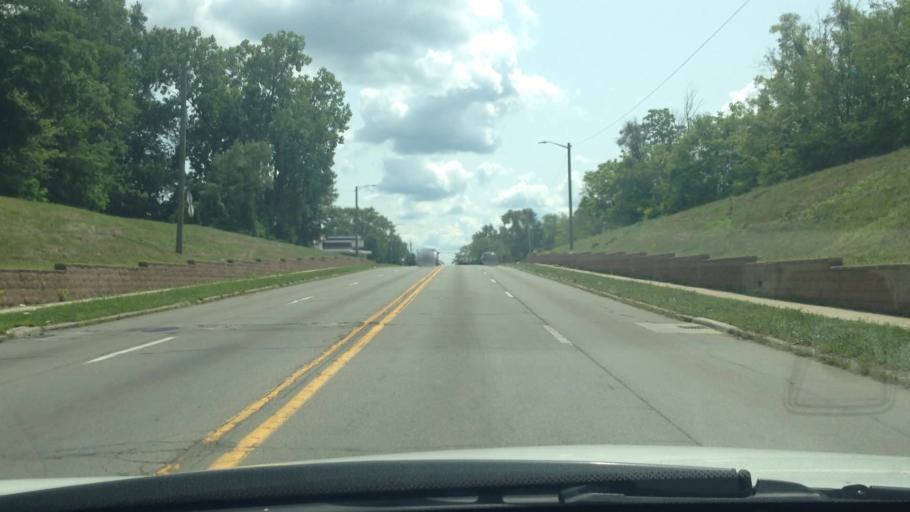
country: US
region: Michigan
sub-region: Wayne County
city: Inkster
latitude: 42.2905
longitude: -83.3100
